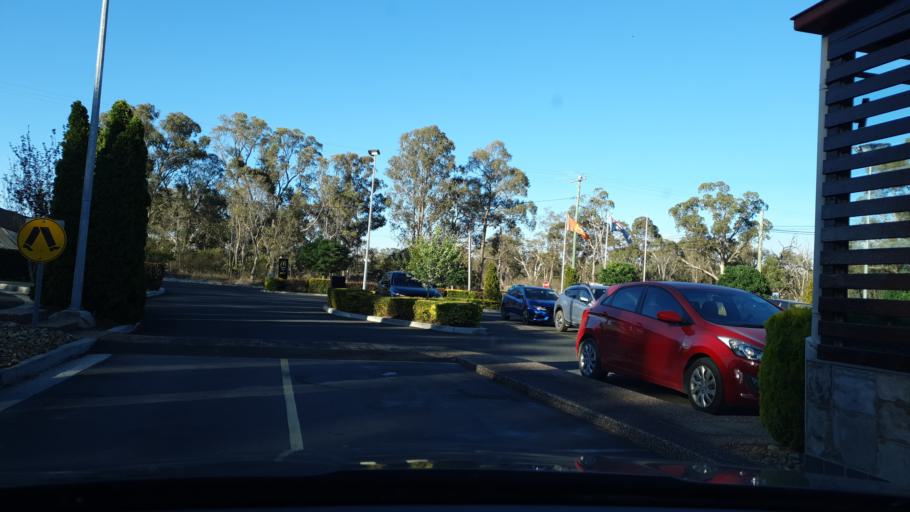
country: AU
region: Queensland
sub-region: Southern Downs
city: Stanthorpe
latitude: -28.6308
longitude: 151.9537
